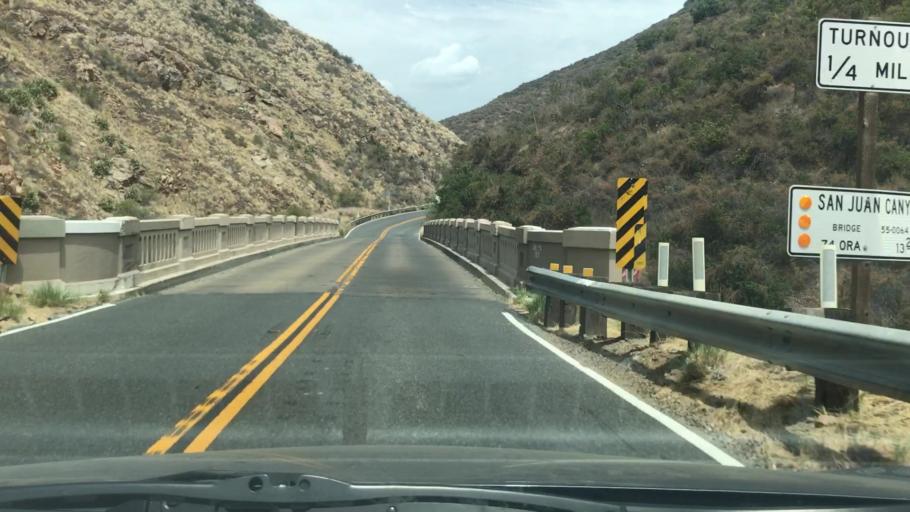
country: US
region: California
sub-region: Orange County
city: Coto De Caza
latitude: 33.5903
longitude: -117.5020
